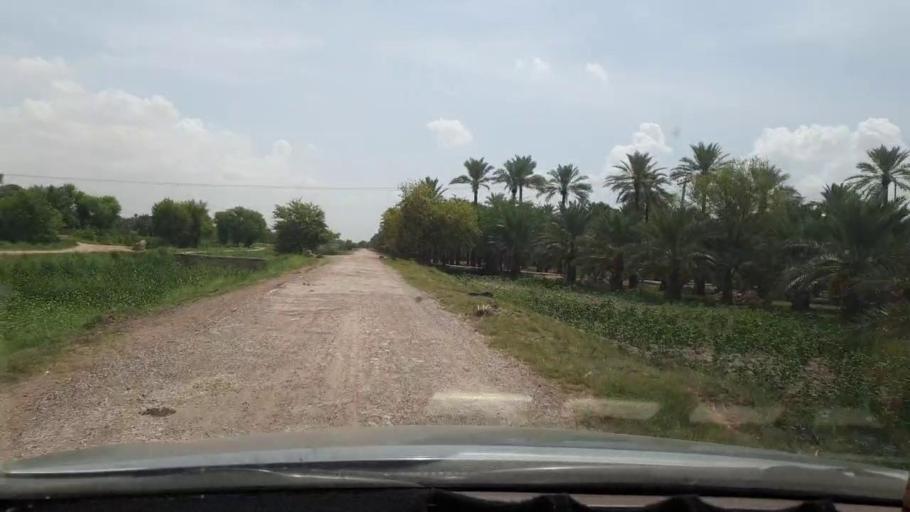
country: PK
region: Sindh
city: Khairpur
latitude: 27.4594
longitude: 68.7918
